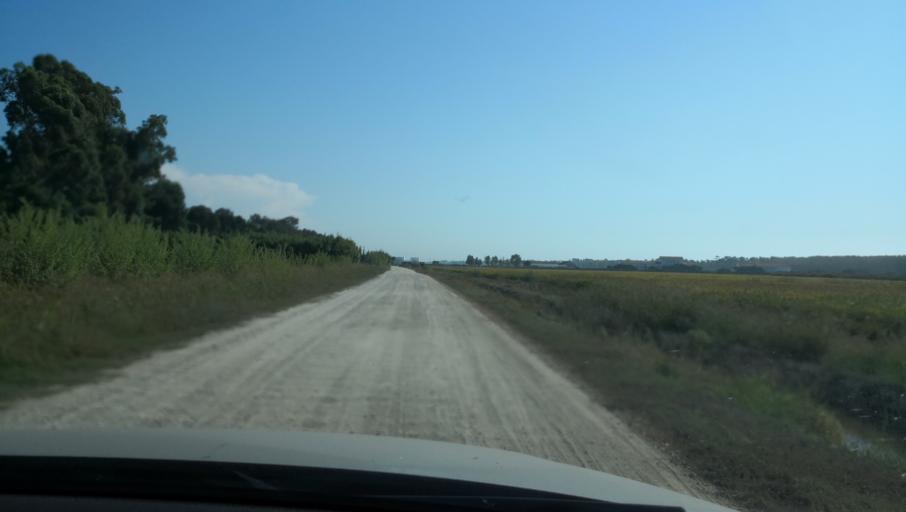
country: PT
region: Setubal
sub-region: Setubal
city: Setubal
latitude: 38.3875
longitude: -8.7894
